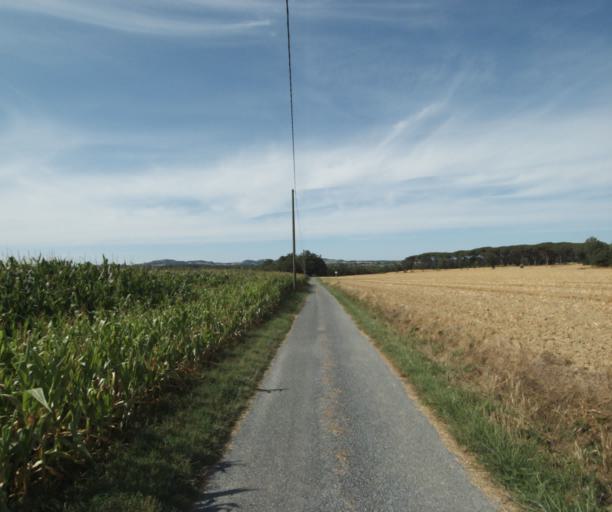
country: FR
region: Midi-Pyrenees
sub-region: Departement du Tarn
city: Soual
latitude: 43.5158
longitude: 2.0876
